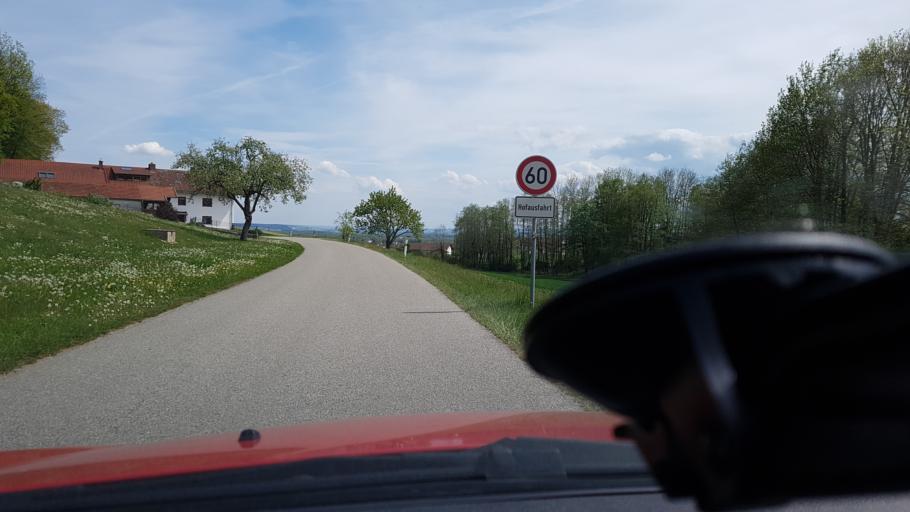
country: DE
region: Bavaria
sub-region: Lower Bavaria
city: Ering
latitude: 48.3116
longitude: 13.1207
